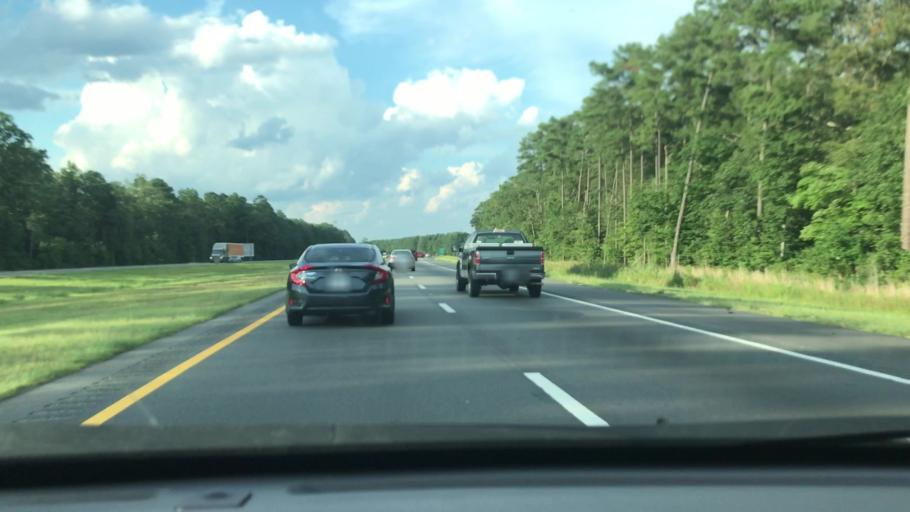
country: US
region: North Carolina
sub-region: Cumberland County
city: Vander
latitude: 35.0154
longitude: -78.8157
